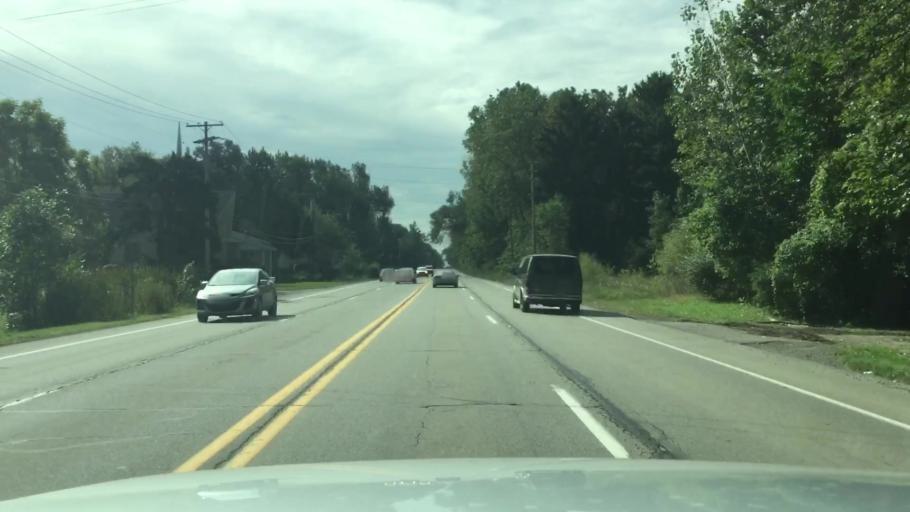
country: US
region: Michigan
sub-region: Wayne County
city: Belleville
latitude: 42.2539
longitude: -83.4865
